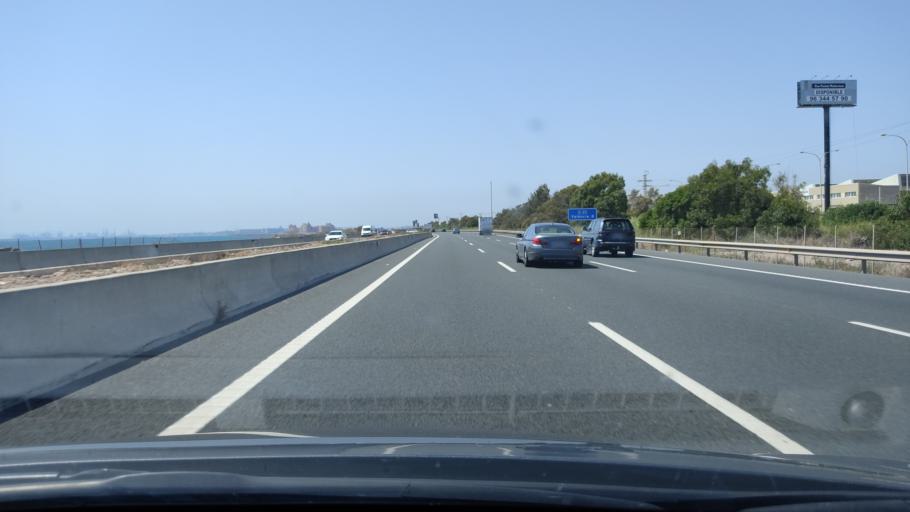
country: ES
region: Valencia
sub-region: Provincia de Valencia
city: Albuixech
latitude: 39.5370
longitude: -0.3074
